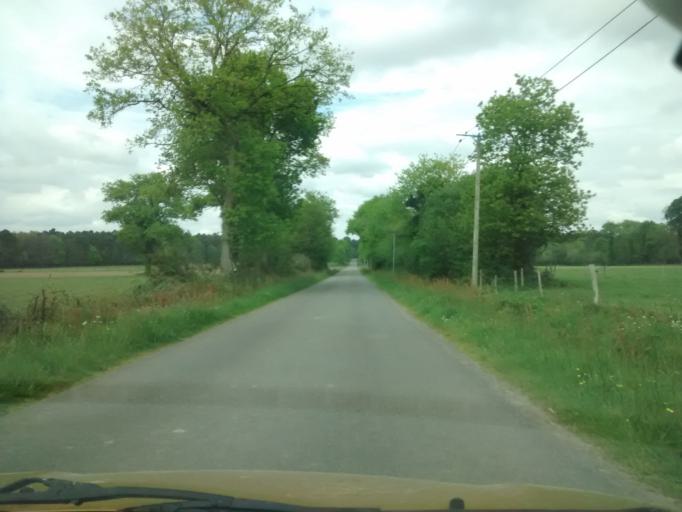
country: FR
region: Brittany
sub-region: Departement du Morbihan
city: Molac
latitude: 47.7318
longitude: -2.4245
